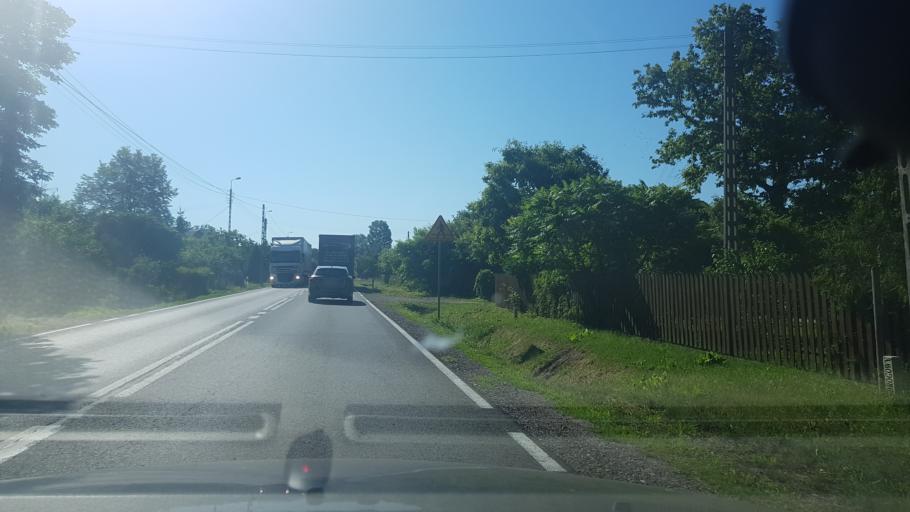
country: PL
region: Masovian Voivodeship
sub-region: Powiat wegrowski
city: Lochow
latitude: 52.5477
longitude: 21.6317
